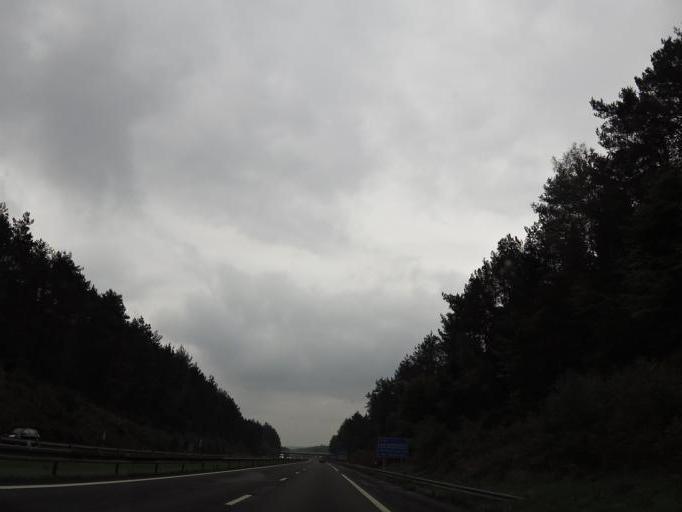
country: FR
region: Lorraine
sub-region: Departement de la Moselle
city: Longeville-les-Saint-Avold
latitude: 49.1351
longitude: 6.6484
